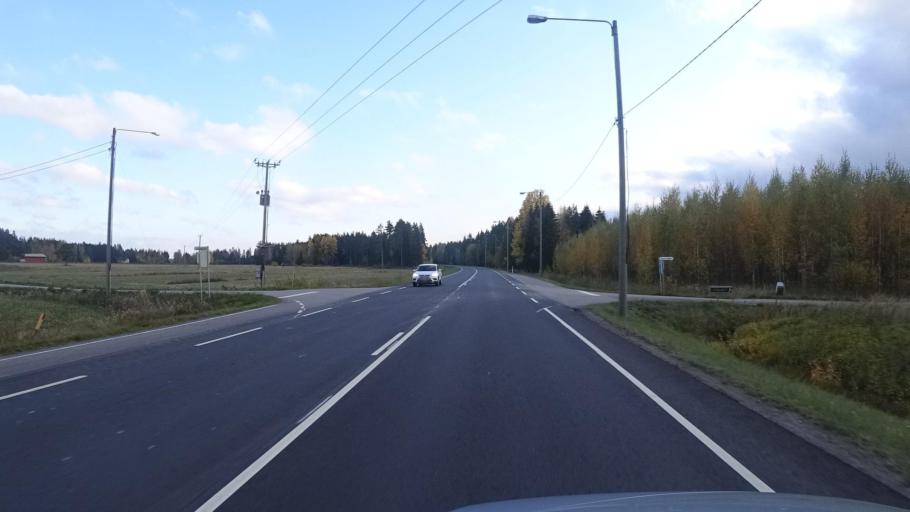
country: FI
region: Satakunta
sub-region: Rauma
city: Koeylioe
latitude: 61.0969
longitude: 22.2379
